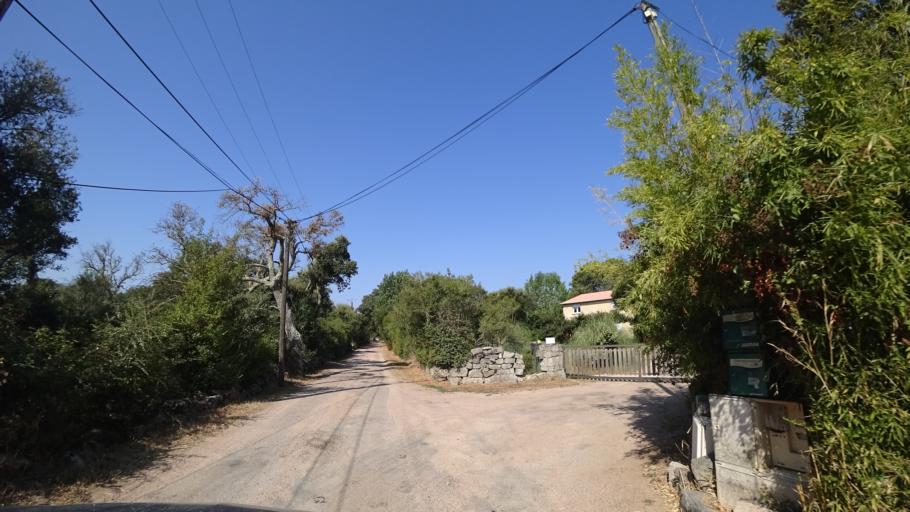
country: FR
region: Corsica
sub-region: Departement de la Corse-du-Sud
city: Porto-Vecchio
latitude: 41.5669
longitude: 9.2138
